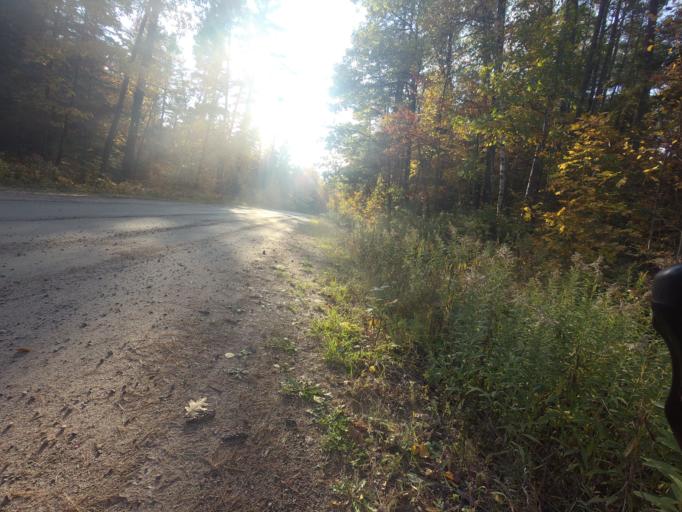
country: CA
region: Ontario
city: Deep River
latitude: 45.8900
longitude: -77.6351
